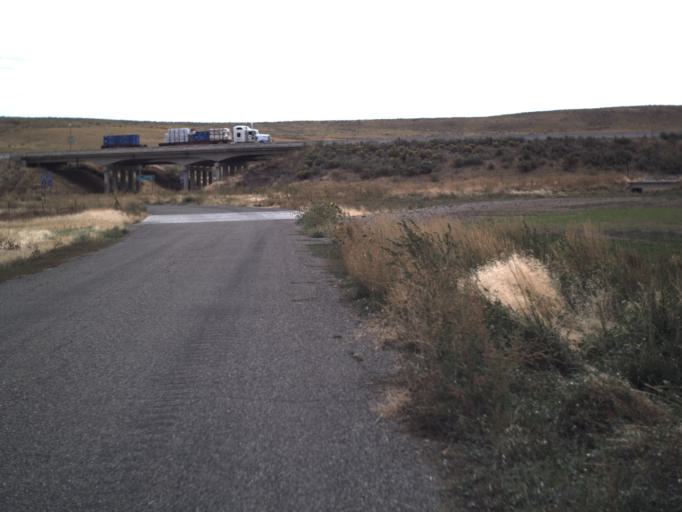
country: US
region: Utah
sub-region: Box Elder County
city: Garland
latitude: 41.8868
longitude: -112.4902
